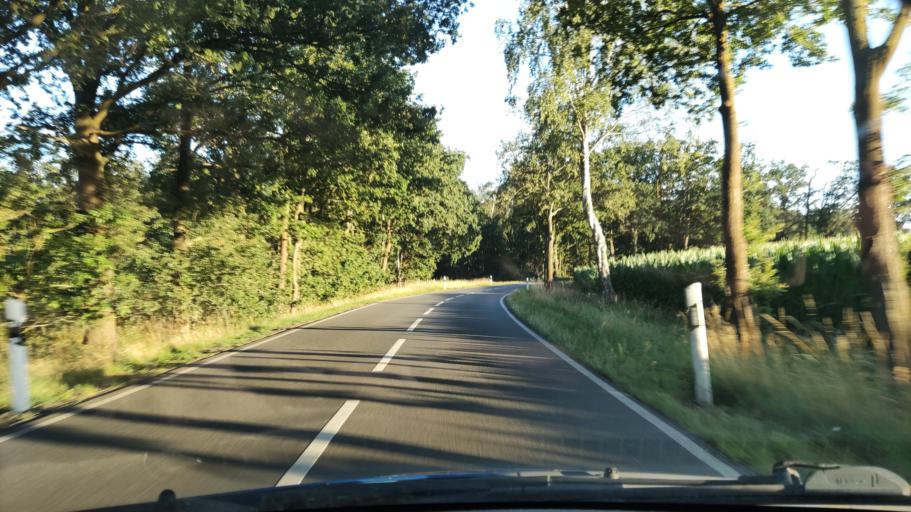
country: DE
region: Lower Saxony
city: Jameln
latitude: 53.0336
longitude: 11.1297
